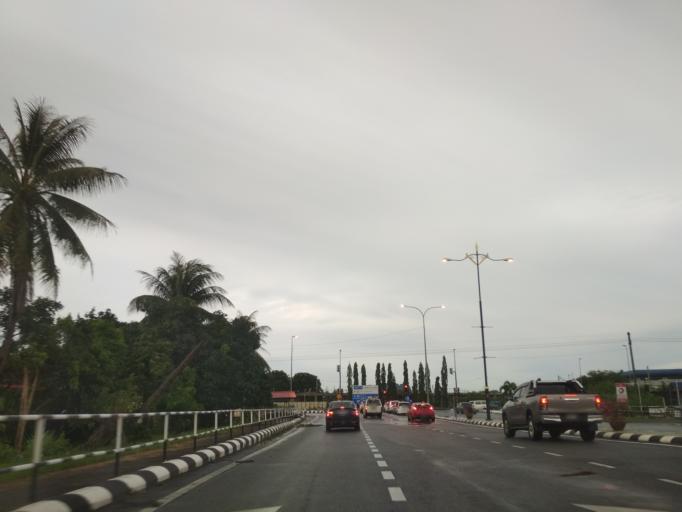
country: MY
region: Perlis
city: Kangar
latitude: 6.4385
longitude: 100.2086
